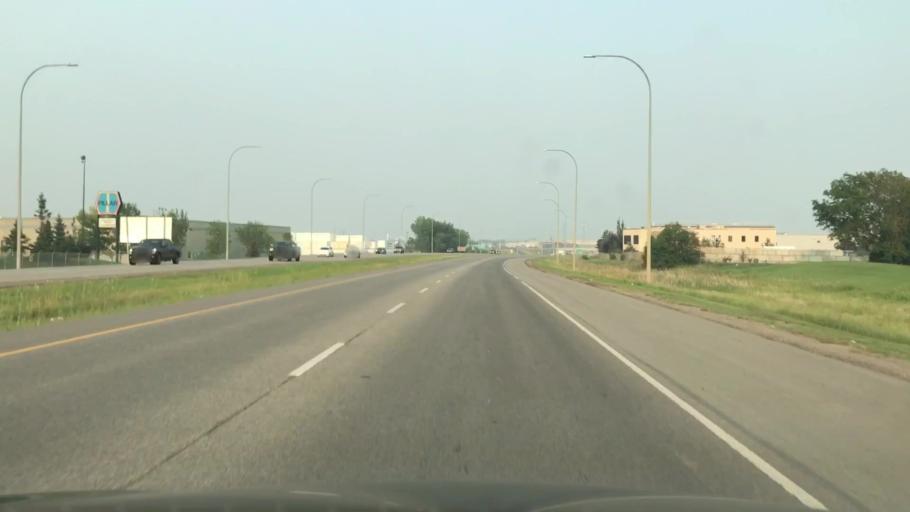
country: CA
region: Alberta
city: Edmonton
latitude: 53.5161
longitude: -113.4060
